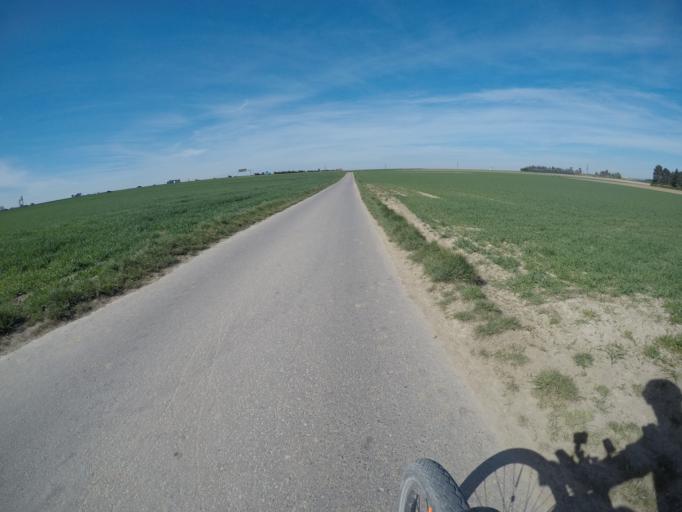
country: DE
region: Baden-Wuerttemberg
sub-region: Regierungsbezirk Stuttgart
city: Korntal
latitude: 48.8575
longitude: 9.1291
